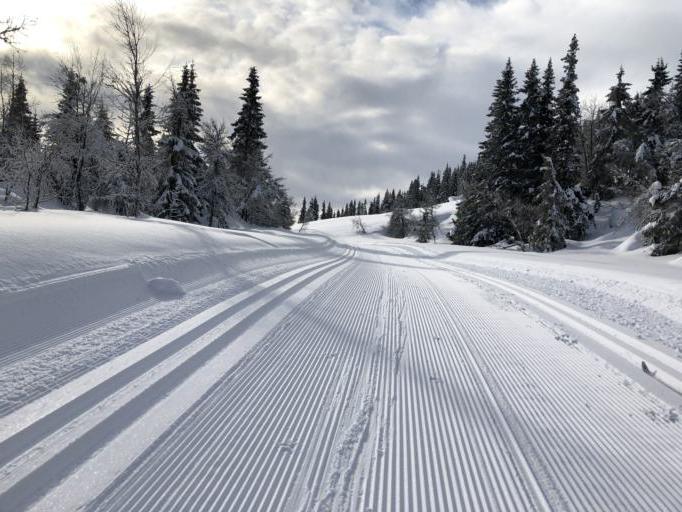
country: NO
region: Oppland
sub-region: Gausdal
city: Segalstad bru
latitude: 61.3197
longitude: 10.0579
